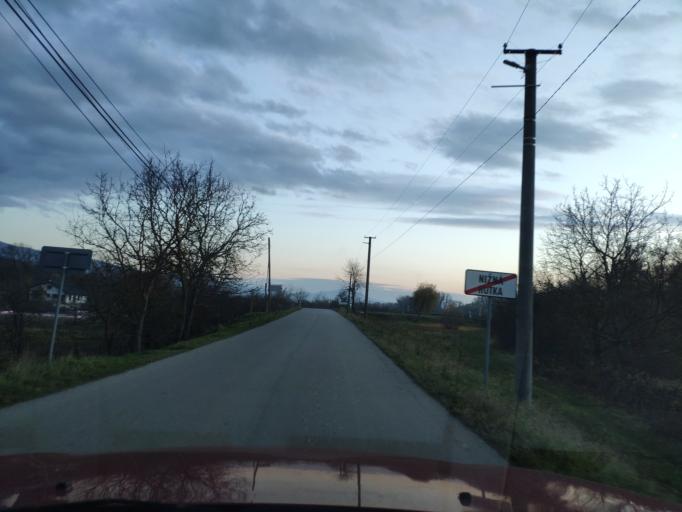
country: SK
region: Kosicky
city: Kosice
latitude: 48.6586
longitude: 21.3563
